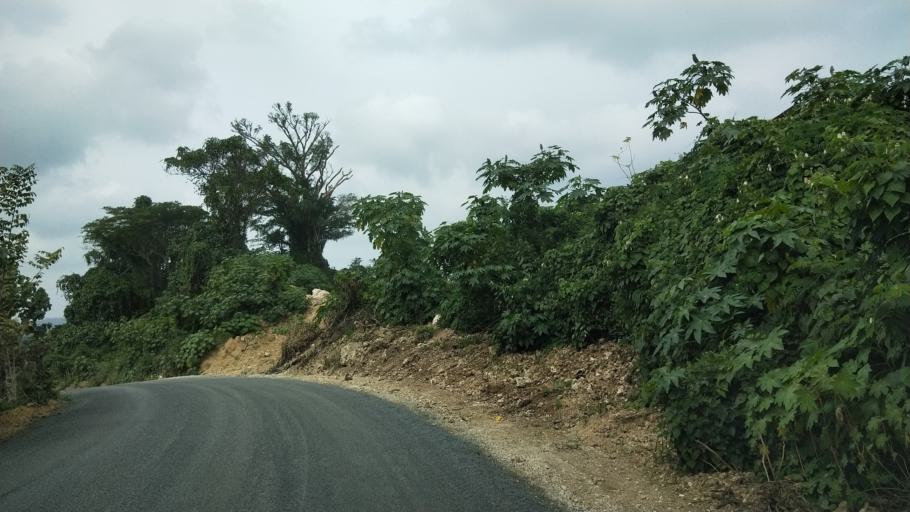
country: VU
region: Shefa
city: Port-Vila
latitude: -17.7721
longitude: 168.3746
